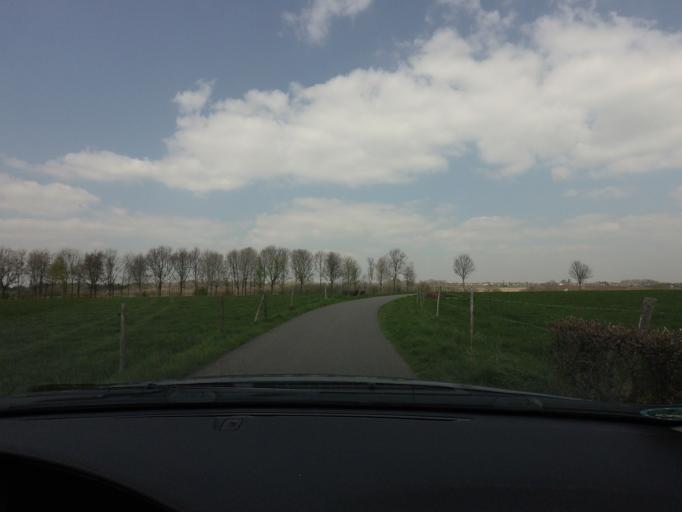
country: BE
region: Flanders
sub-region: Provincie Limburg
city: Sint-Pieters-Voeren
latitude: 50.7760
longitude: 5.8082
